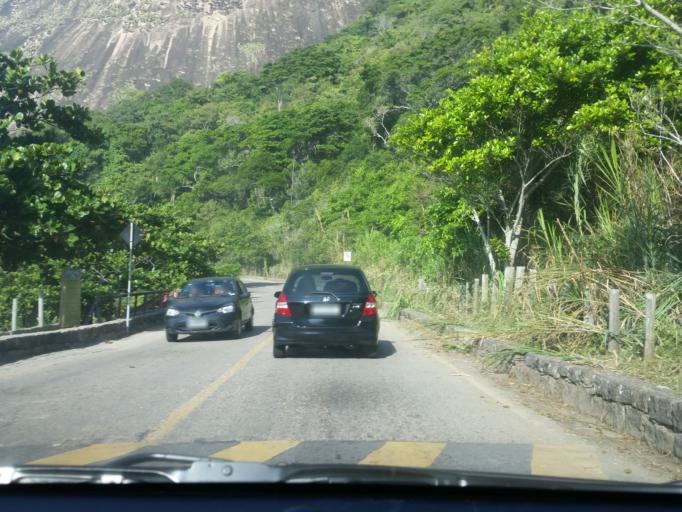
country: BR
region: Rio de Janeiro
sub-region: Nilopolis
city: Nilopolis
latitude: -23.0419
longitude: -43.5075
